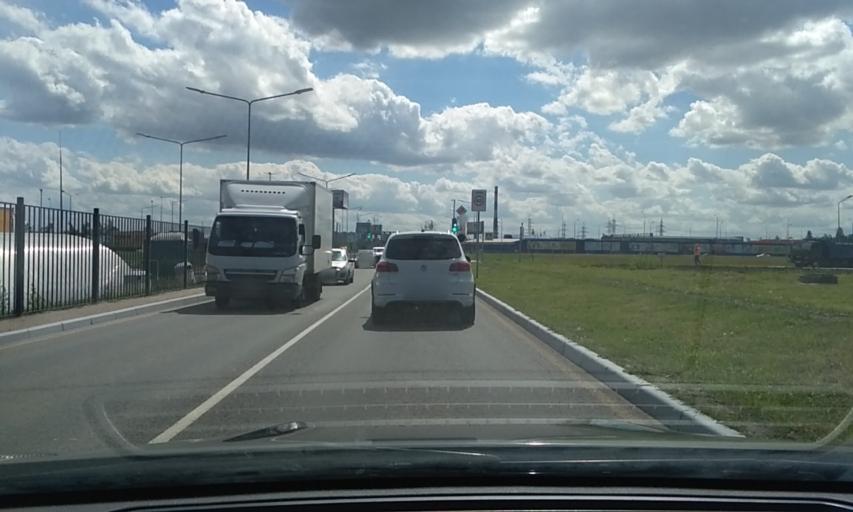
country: RU
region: Leningrad
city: Rybatskoye
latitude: 59.8921
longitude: 30.5087
